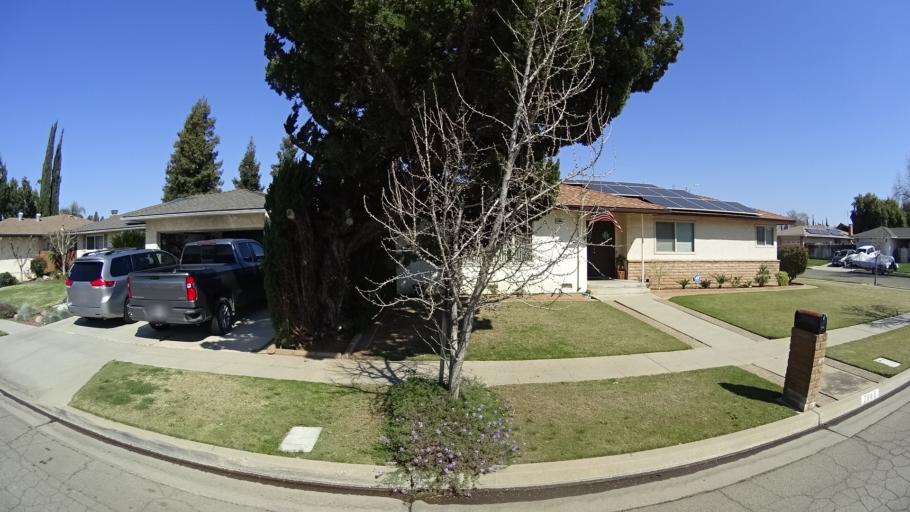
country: US
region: California
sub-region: Fresno County
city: Clovis
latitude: 36.8351
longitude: -119.7382
